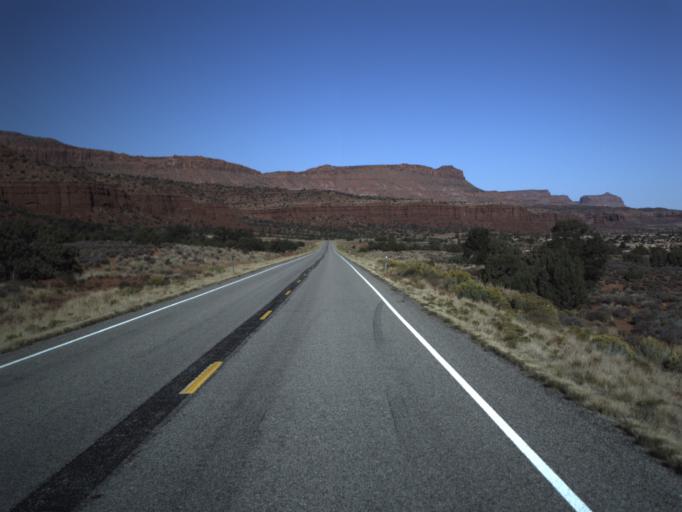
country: US
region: Utah
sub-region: San Juan County
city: Blanding
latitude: 37.6743
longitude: -110.2072
